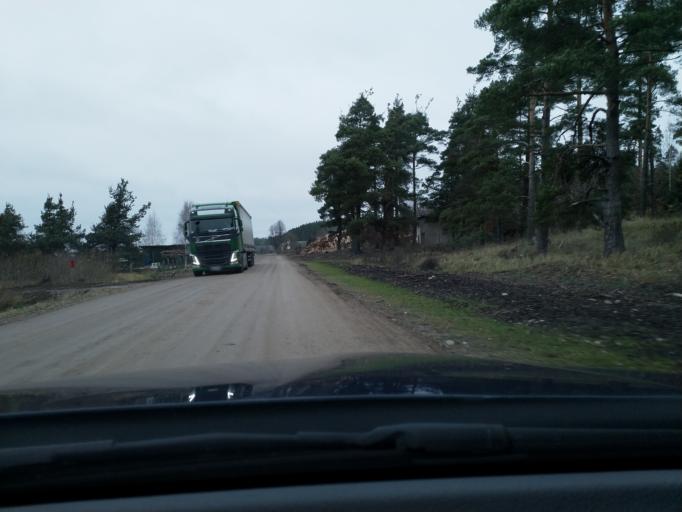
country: LV
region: Ventspils Rajons
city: Piltene
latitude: 57.1284
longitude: 21.8016
